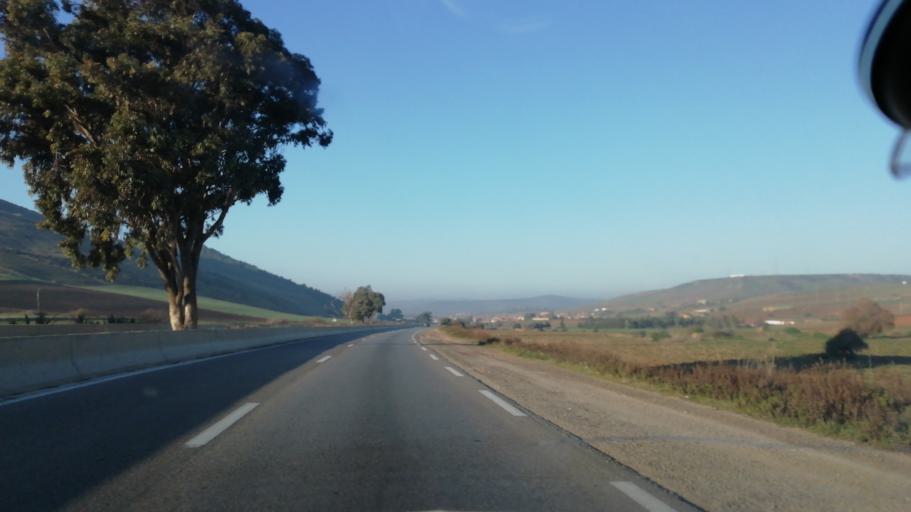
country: DZ
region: Ain Temouchent
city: Beni Saf
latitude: 35.2288
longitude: -1.3841
